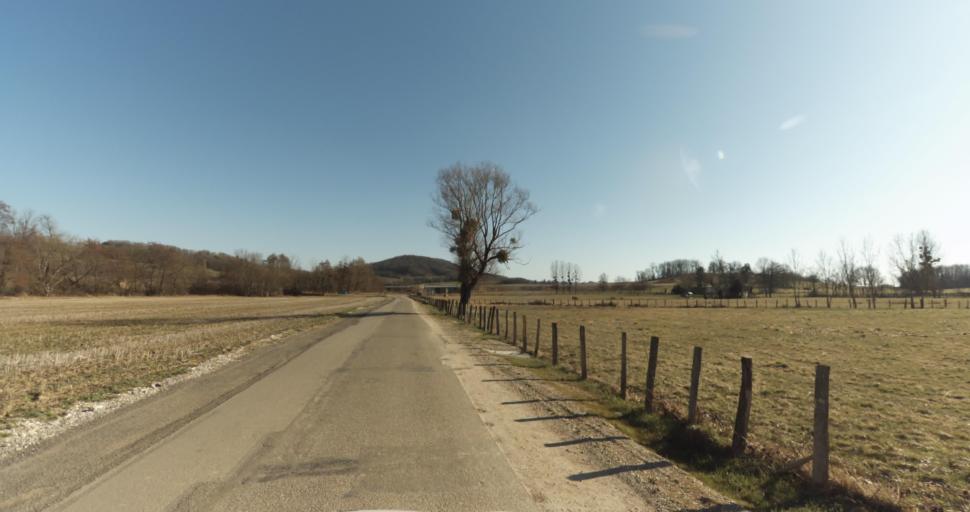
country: FR
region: Franche-Comte
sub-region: Departement du Jura
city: Montmorot
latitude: 46.7012
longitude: 5.5308
